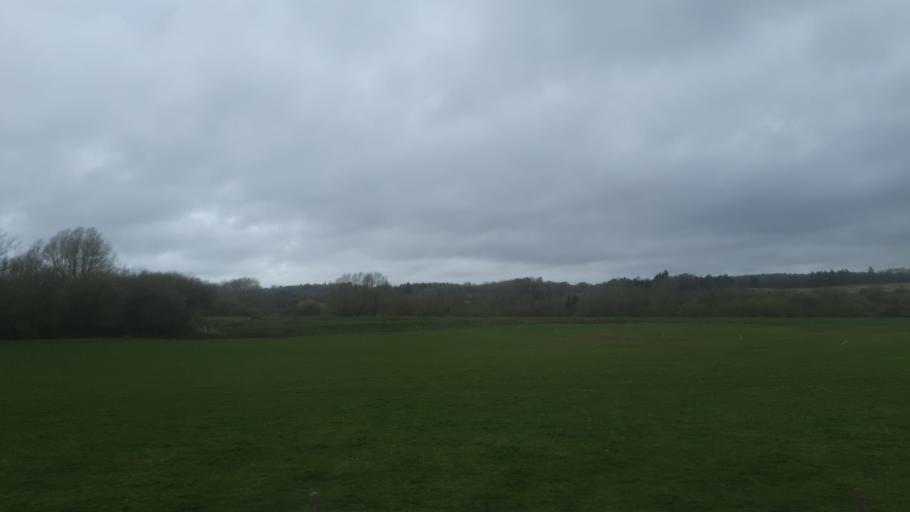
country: GB
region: England
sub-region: West Sussex
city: Pulborough
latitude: 50.9508
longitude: -0.5236
